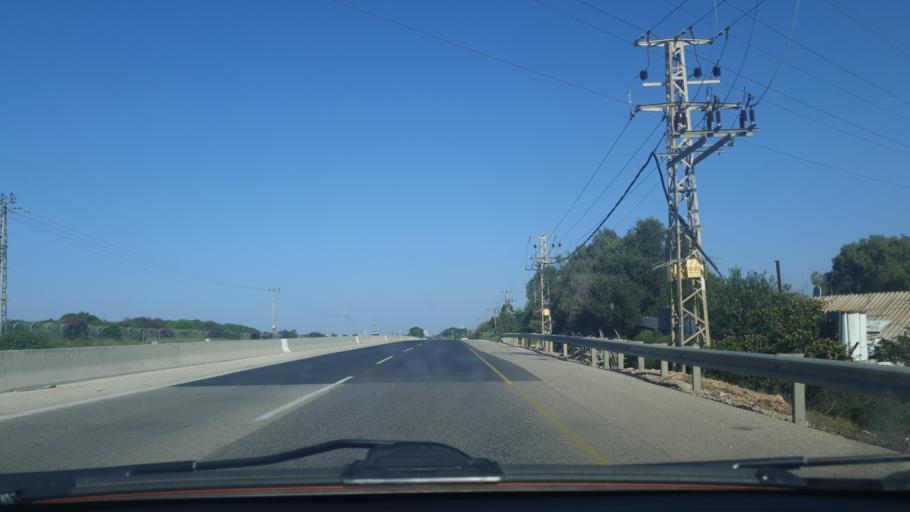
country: IL
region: Central District
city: Bet Dagan
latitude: 31.9851
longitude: 34.8325
